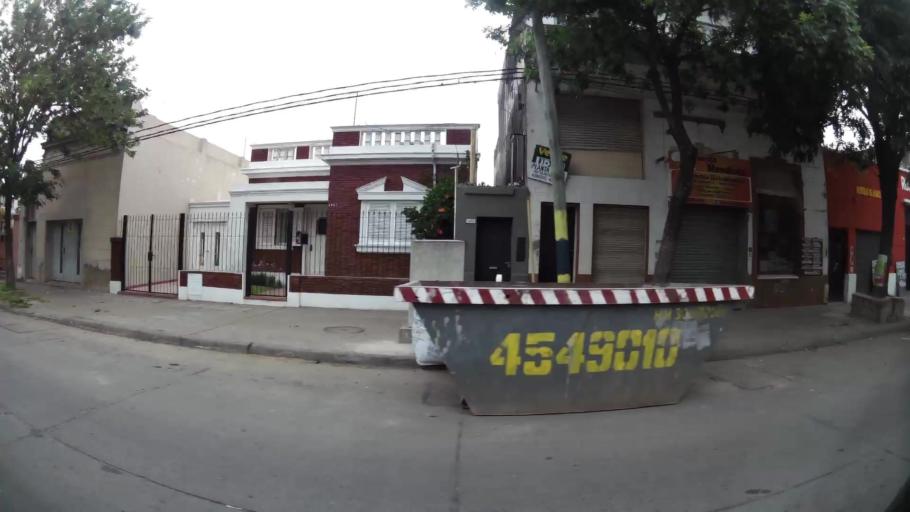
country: AR
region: Santa Fe
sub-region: Departamento de Rosario
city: Rosario
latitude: -32.9154
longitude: -60.6901
